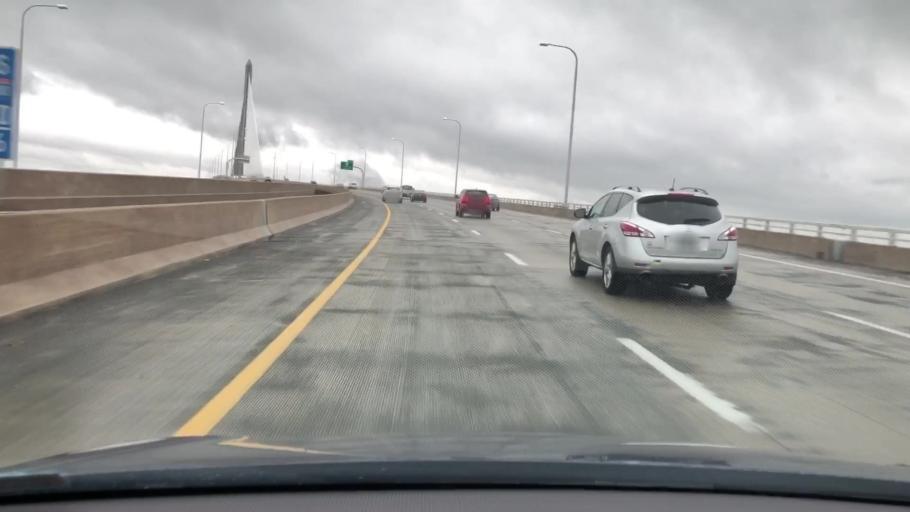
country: US
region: Ohio
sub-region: Lucas County
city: Oregon
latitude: 41.6655
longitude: -83.5146
